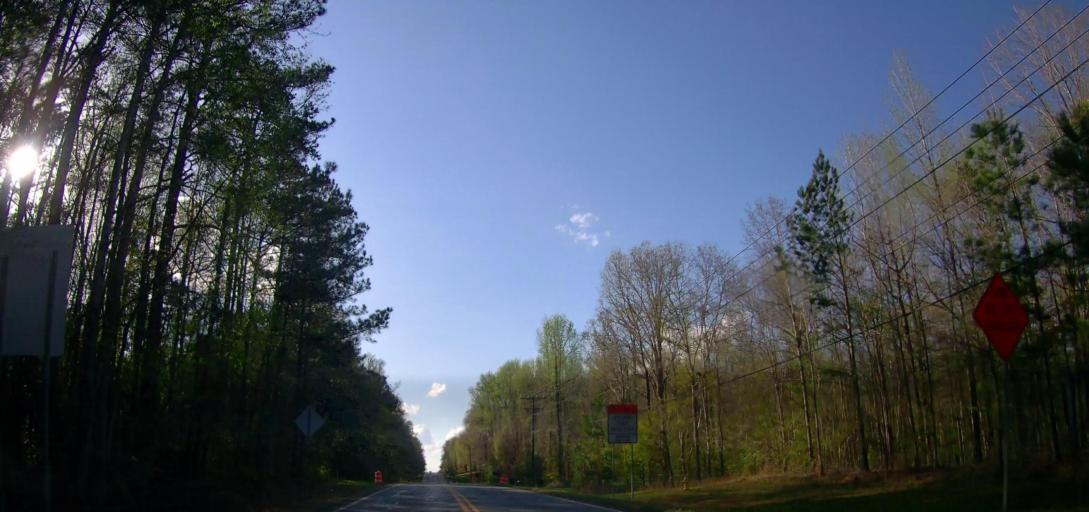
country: US
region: Georgia
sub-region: Putnam County
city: Eatonton
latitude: 33.1663
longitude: -83.3810
